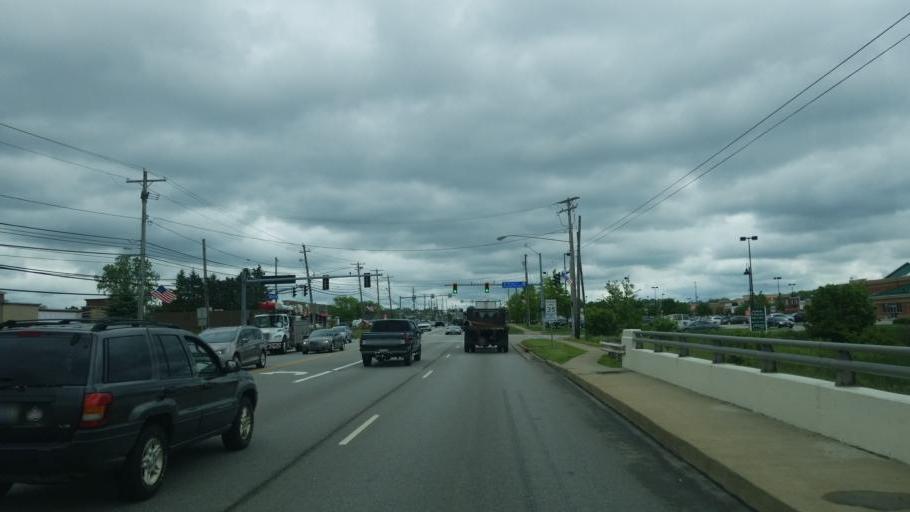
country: US
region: Ohio
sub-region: Medina County
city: Brunswick
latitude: 41.2382
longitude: -81.8115
